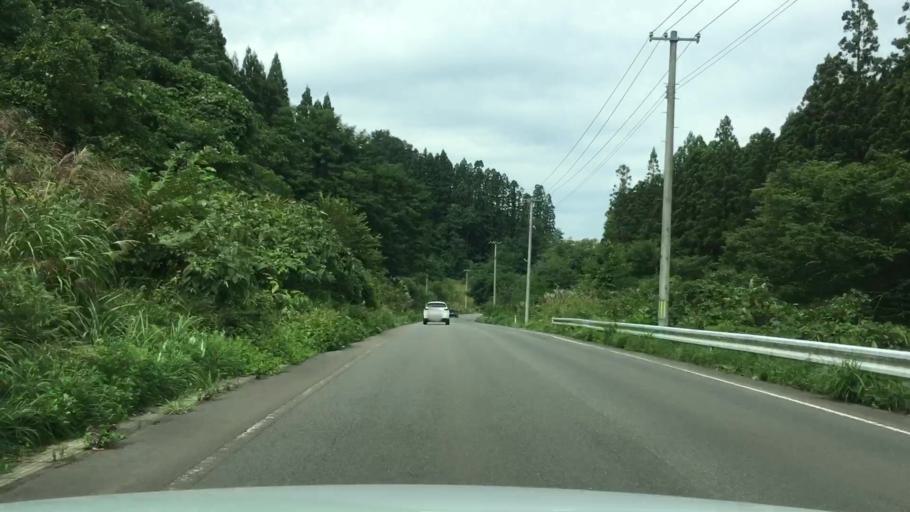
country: JP
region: Aomori
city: Shimokizukuri
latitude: 40.7429
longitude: 140.2431
